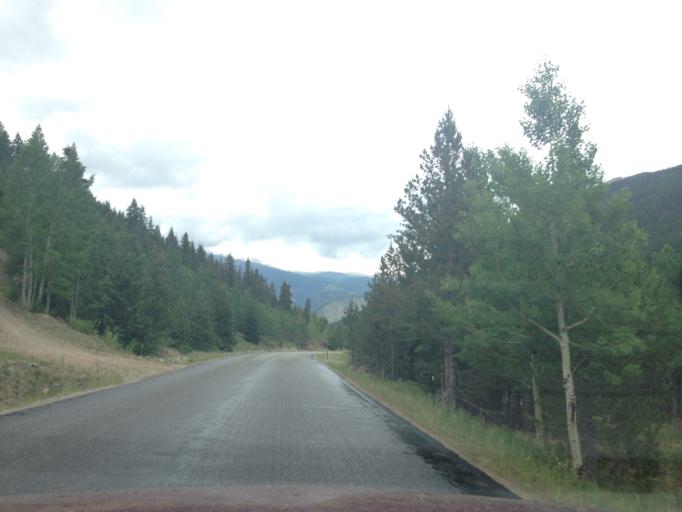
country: US
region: Colorado
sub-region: Clear Creek County
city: Georgetown
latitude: 39.6970
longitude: -105.6956
